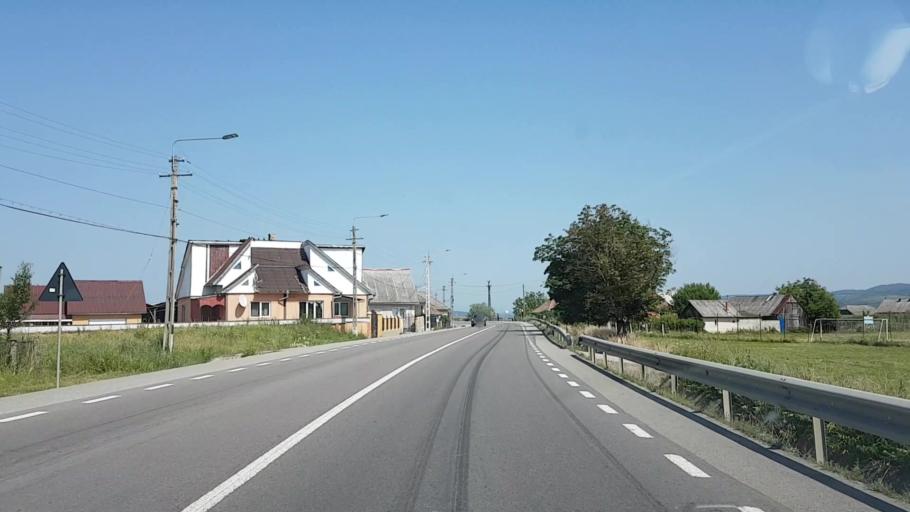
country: RO
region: Bistrita-Nasaud
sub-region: Comuna Petru Rares
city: Reteag
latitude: 47.1972
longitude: 24.0223
